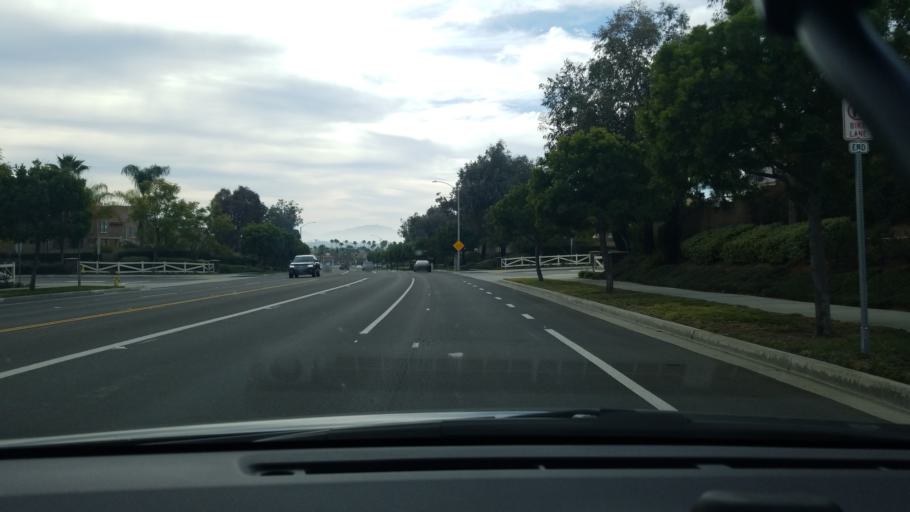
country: US
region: California
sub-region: Riverside County
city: Murrieta Hot Springs
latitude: 33.5568
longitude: -117.1108
